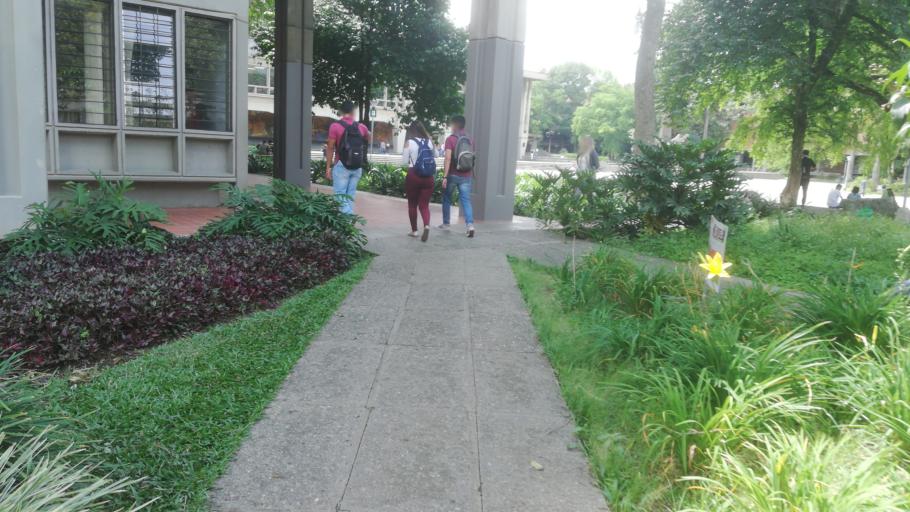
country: CO
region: Antioquia
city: Medellin
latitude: 6.2678
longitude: -75.5684
